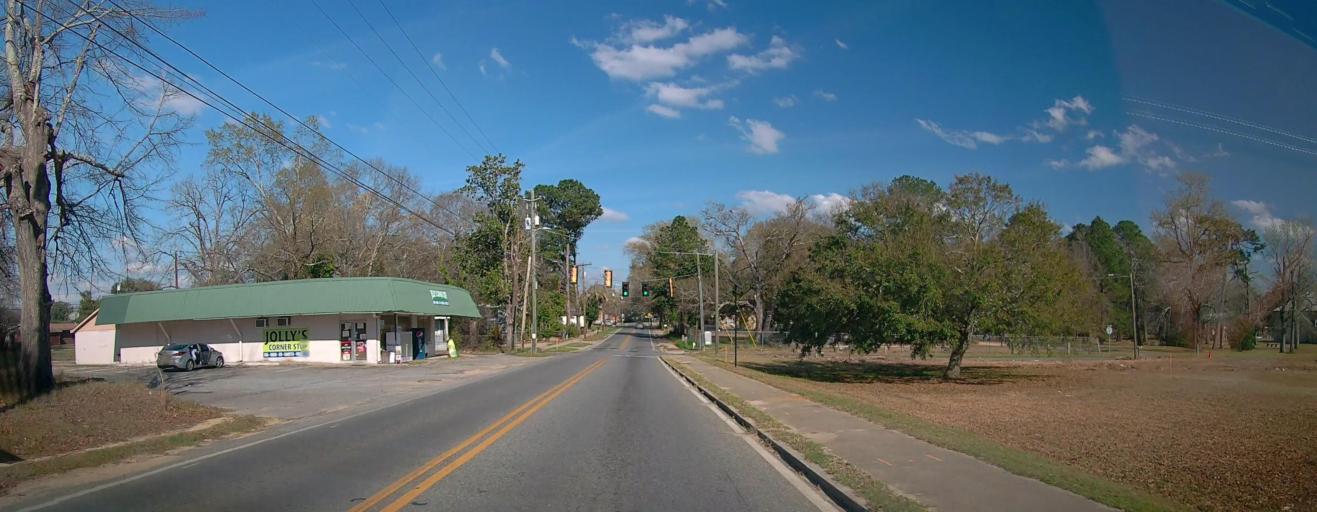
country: US
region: Georgia
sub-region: Laurens County
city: Dublin
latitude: 32.5422
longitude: -82.9157
